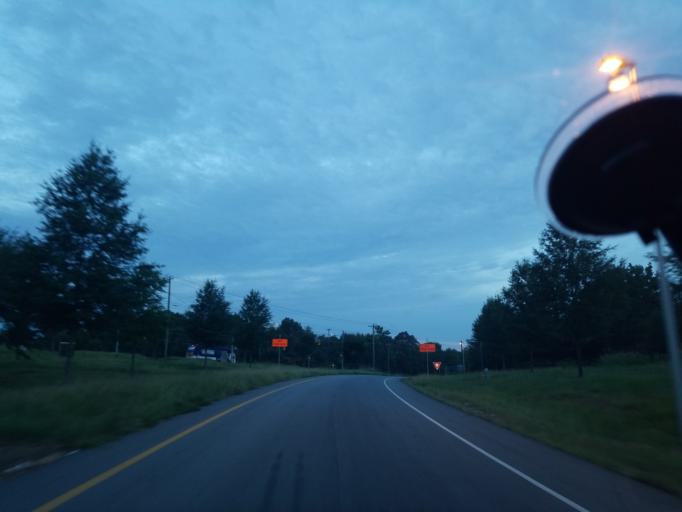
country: US
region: South Carolina
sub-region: Greenville County
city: Greenville
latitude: 34.8589
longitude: -82.3552
